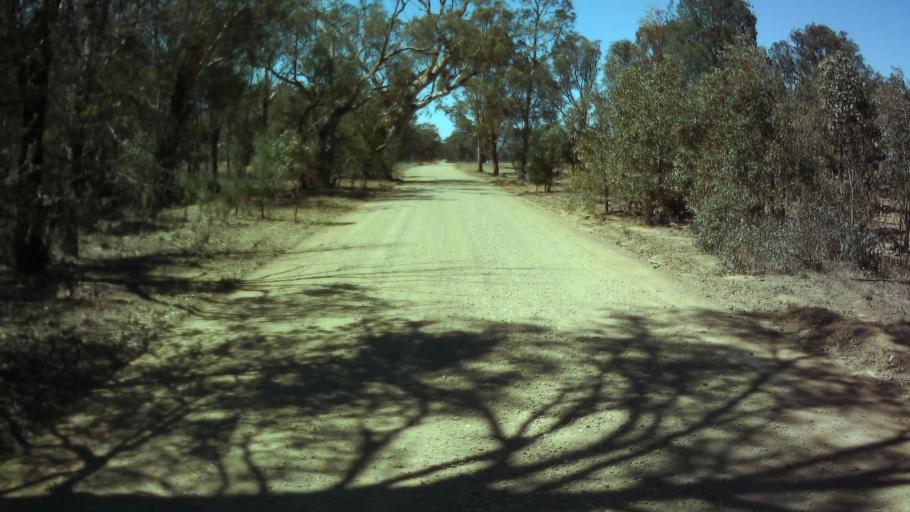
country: AU
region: New South Wales
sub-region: Weddin
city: Grenfell
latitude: -33.8637
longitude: 148.0876
